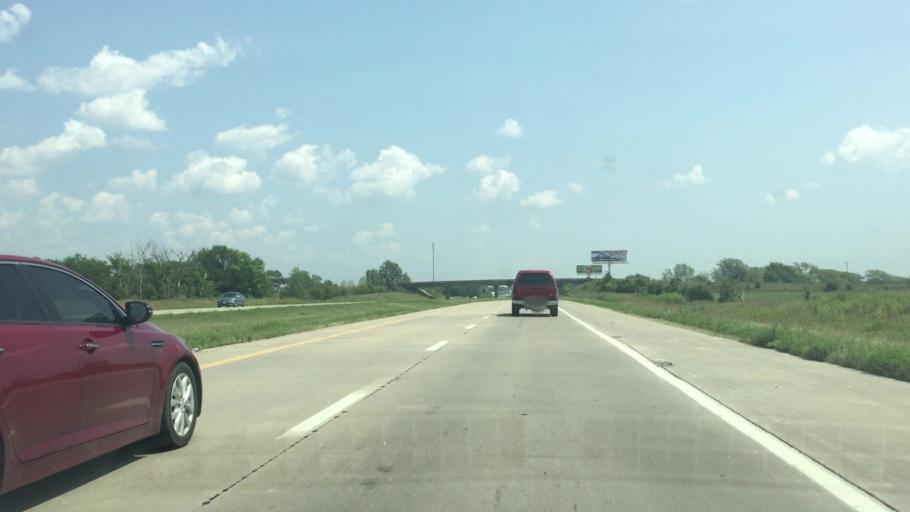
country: US
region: Kansas
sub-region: Franklin County
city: Wellsville
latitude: 38.6828
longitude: -95.1244
